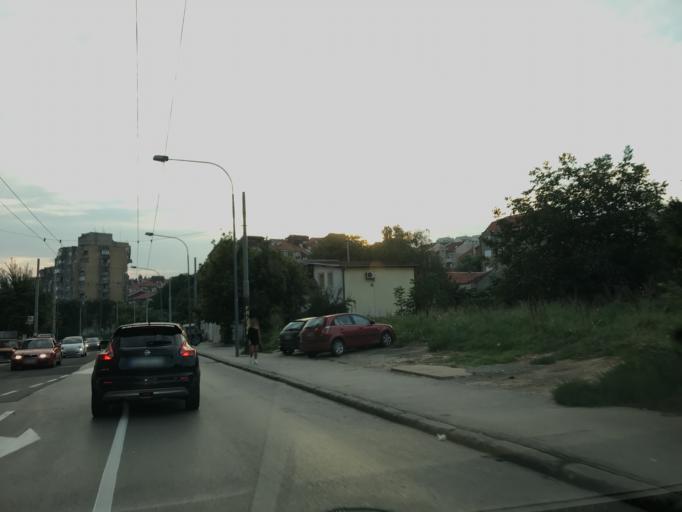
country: RS
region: Central Serbia
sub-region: Belgrade
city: Palilula
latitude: 44.7882
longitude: 20.5055
